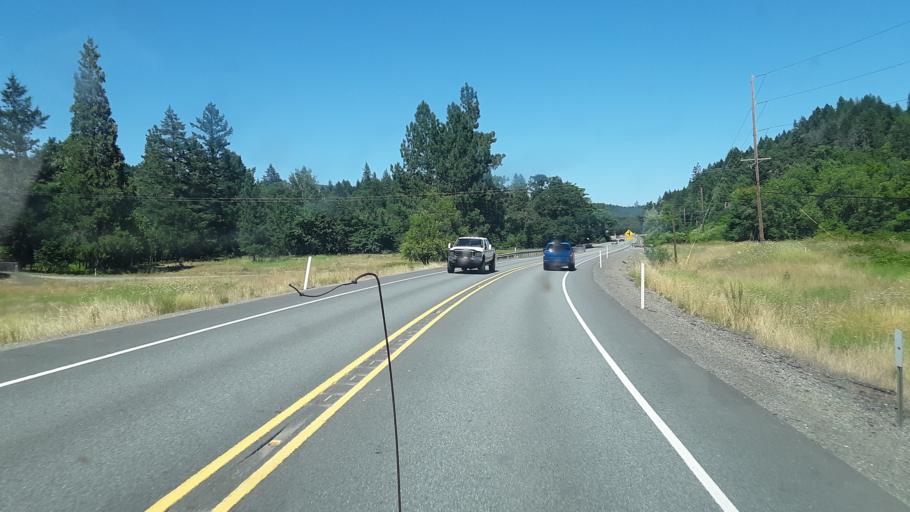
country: US
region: Oregon
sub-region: Josephine County
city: Redwood
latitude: 42.3762
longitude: -123.4984
